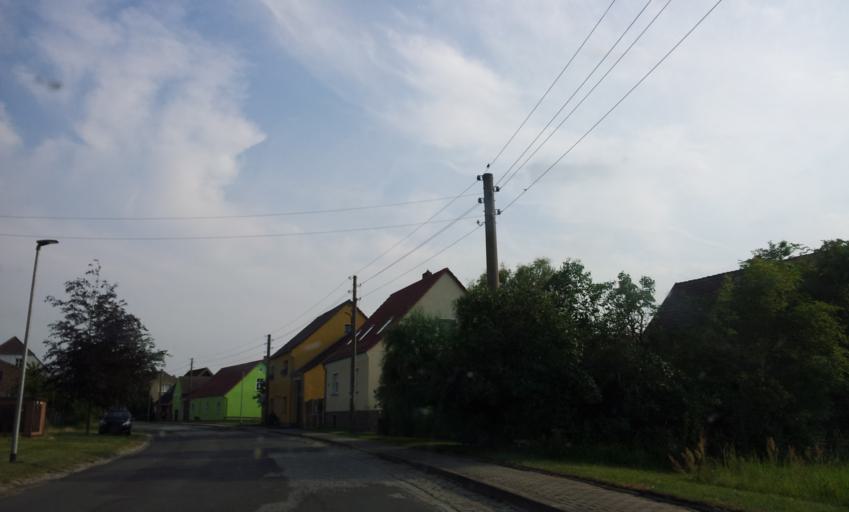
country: DE
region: Brandenburg
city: Treuenbrietzen
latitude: 52.0784
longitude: 12.9426
